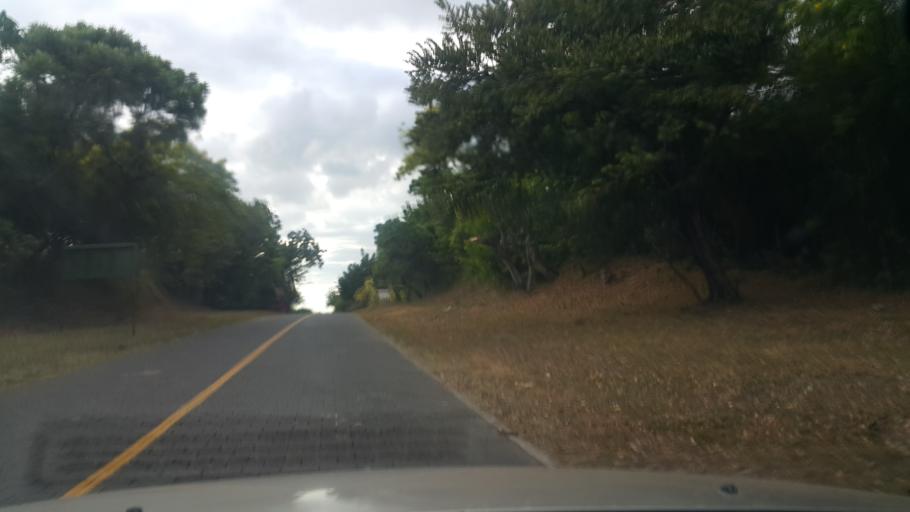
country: NI
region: Rivas
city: Moyogalpa
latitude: 11.4939
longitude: -85.6766
